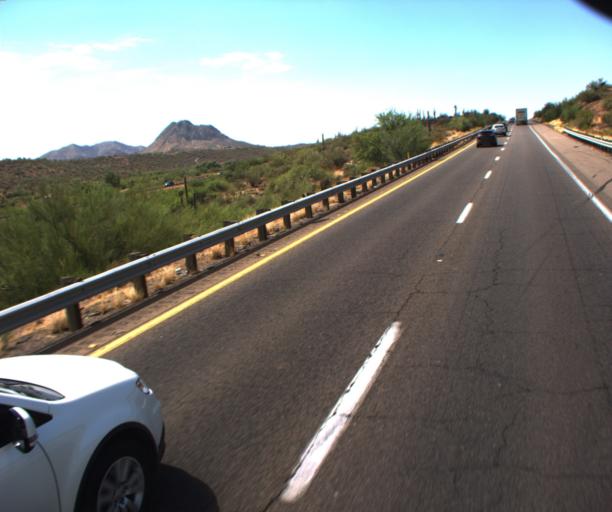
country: US
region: Arizona
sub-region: Maricopa County
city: New River
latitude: 33.9405
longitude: -112.1414
